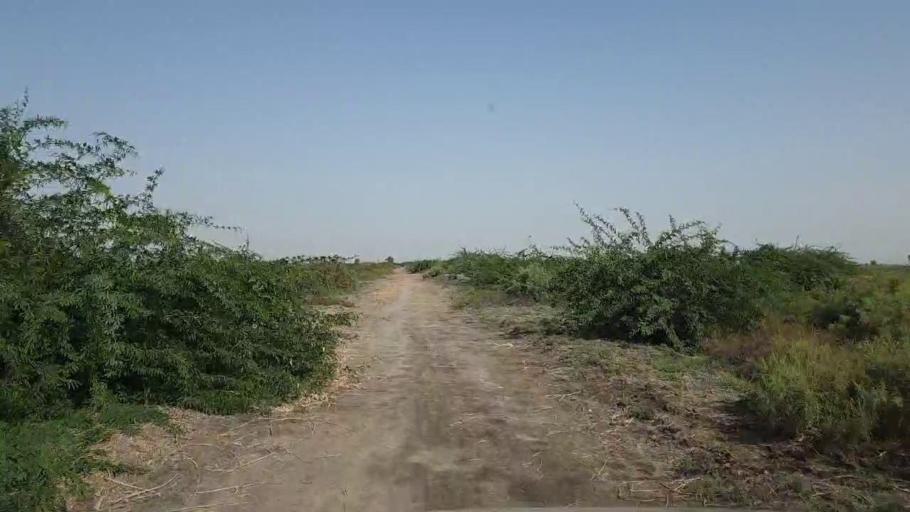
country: PK
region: Sindh
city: Tando Bago
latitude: 24.7148
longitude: 69.0721
